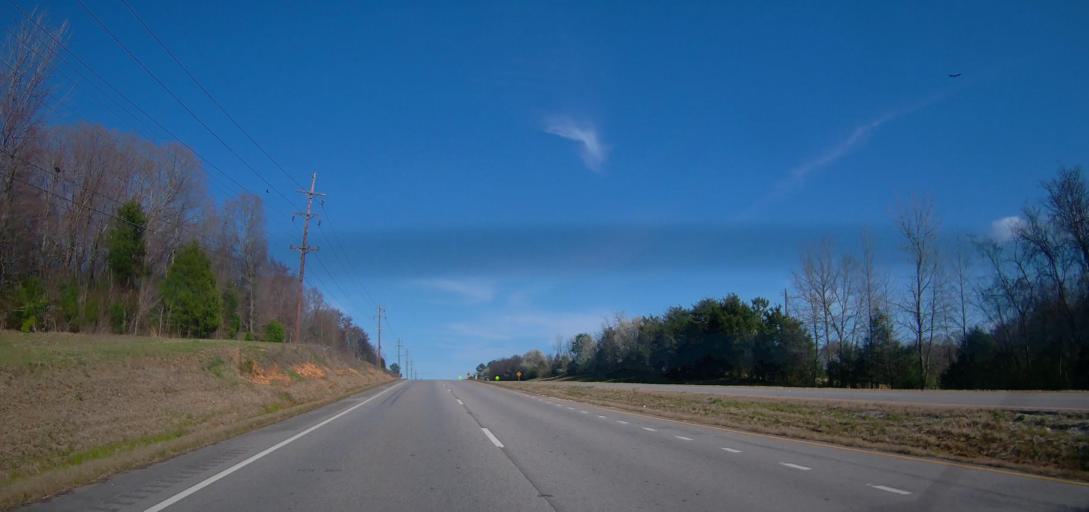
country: US
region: Alabama
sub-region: Lauderdale County
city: Killen
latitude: 34.8598
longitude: -87.5048
